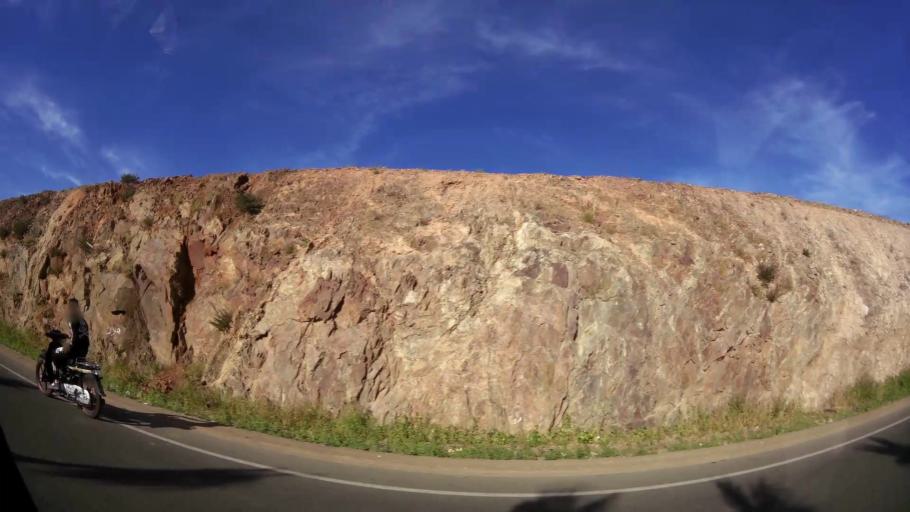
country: MA
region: Marrakech-Tensift-Al Haouz
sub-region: Marrakech
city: Marrakesh
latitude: 31.7033
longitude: -8.0622
